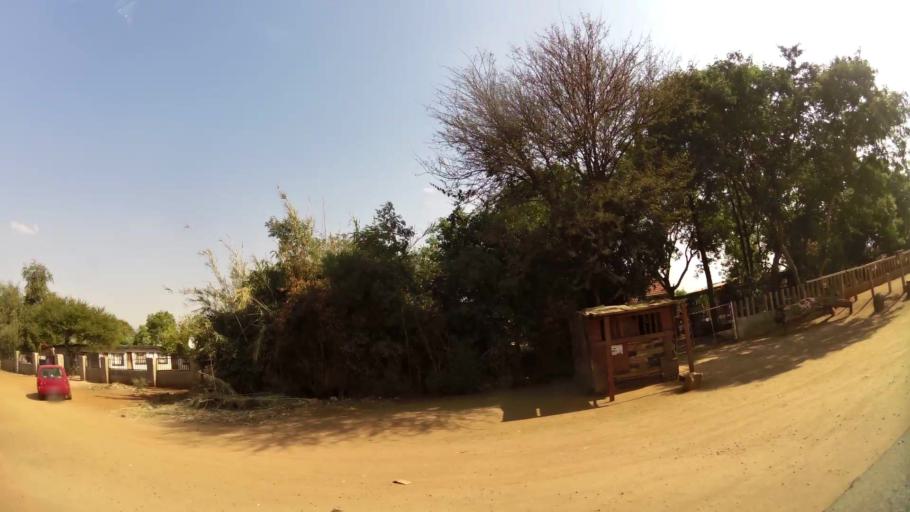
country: ZA
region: North-West
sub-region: Bojanala Platinum District Municipality
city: Mogwase
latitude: -25.3710
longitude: 27.0630
